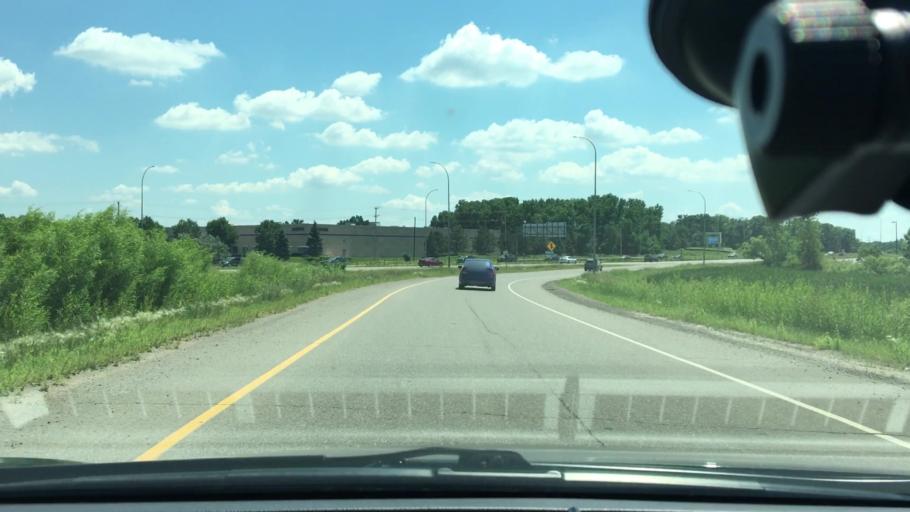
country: US
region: Minnesota
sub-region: Hennepin County
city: Osseo
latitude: 45.0928
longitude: -93.4036
